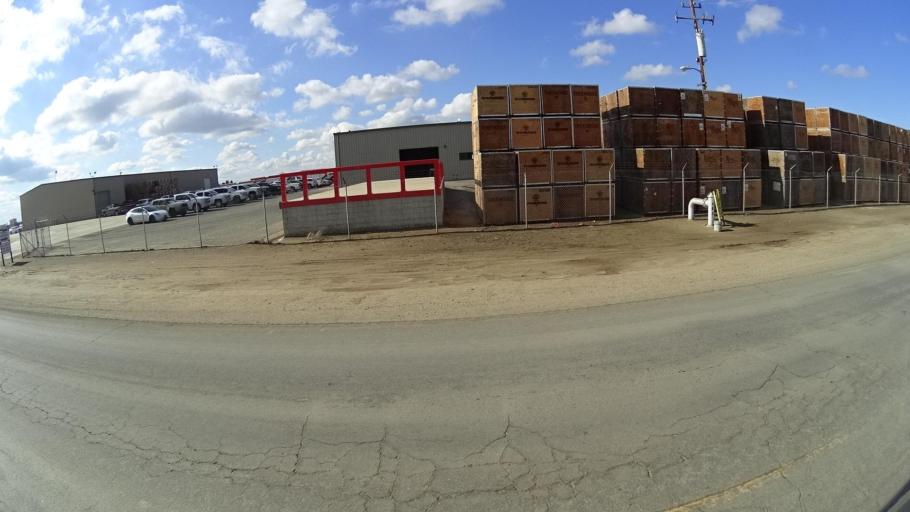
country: US
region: California
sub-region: Kern County
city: McFarland
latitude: 35.6926
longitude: -119.2408
